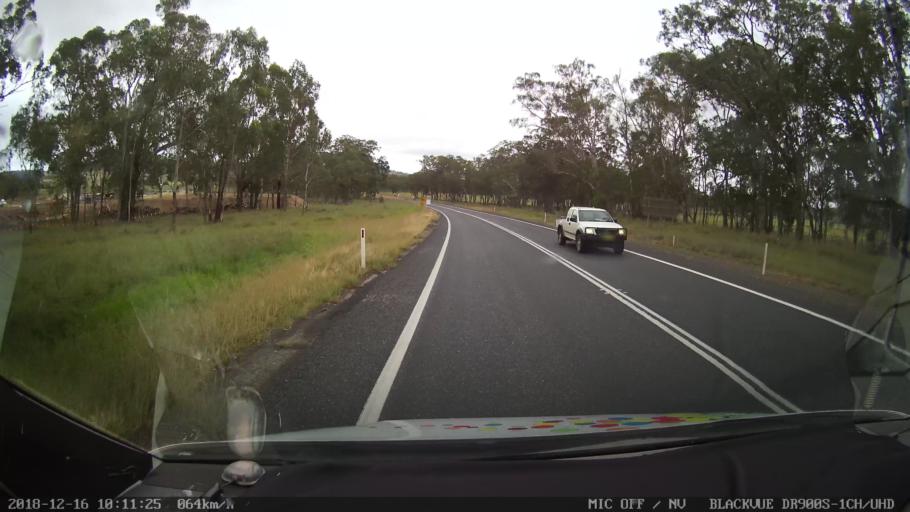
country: AU
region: New South Wales
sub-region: Glen Innes Severn
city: Glen Innes
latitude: -29.3132
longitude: 151.9326
